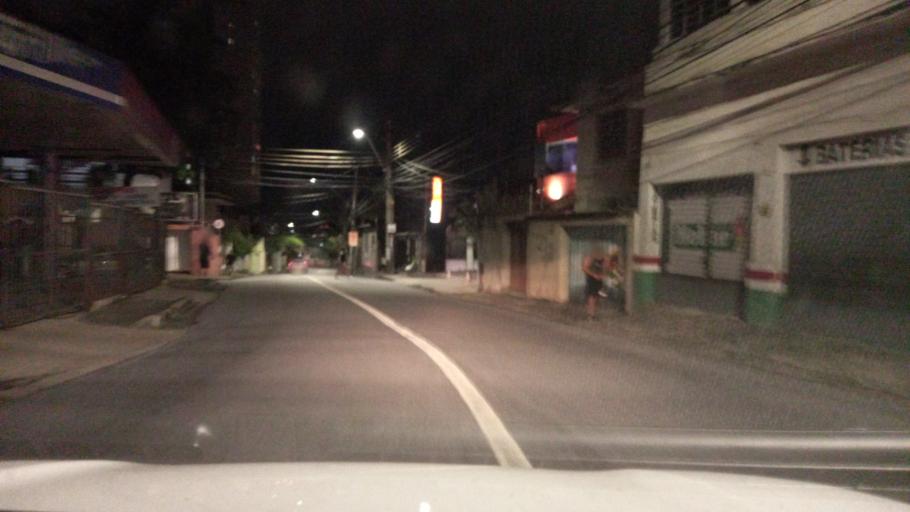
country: BR
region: Minas Gerais
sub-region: Belo Horizonte
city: Belo Horizonte
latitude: -19.9116
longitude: -43.9617
